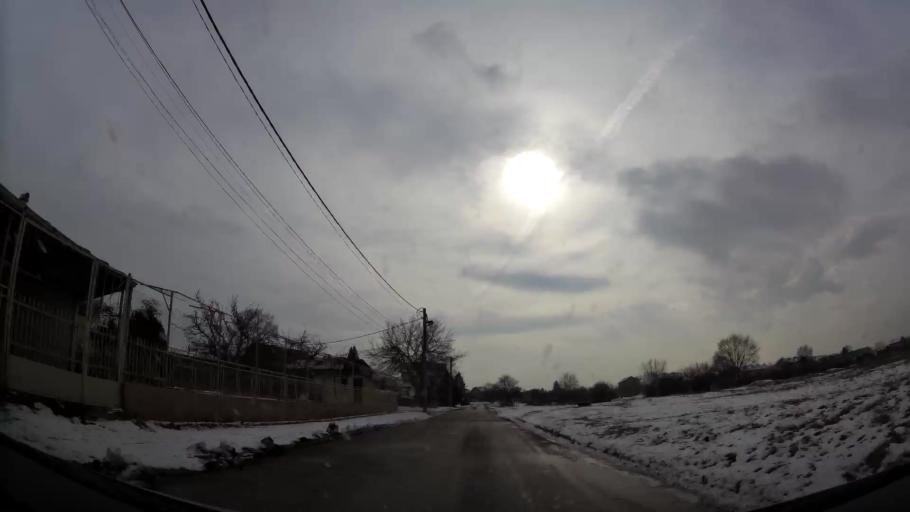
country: BG
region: Sofia-Capital
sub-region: Stolichna Obshtina
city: Sofia
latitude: 42.7161
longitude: 23.4035
